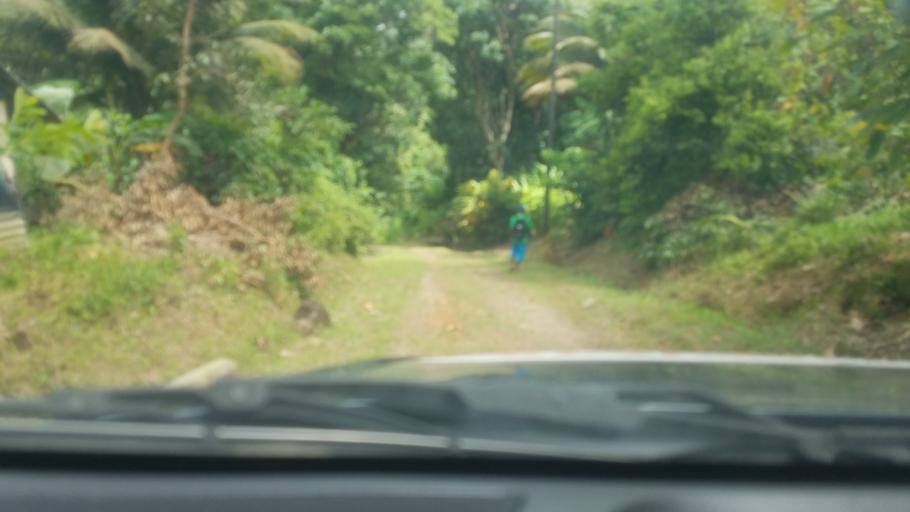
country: LC
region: Micoud Quarter
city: Micoud
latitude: 13.8030
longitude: -60.9518
